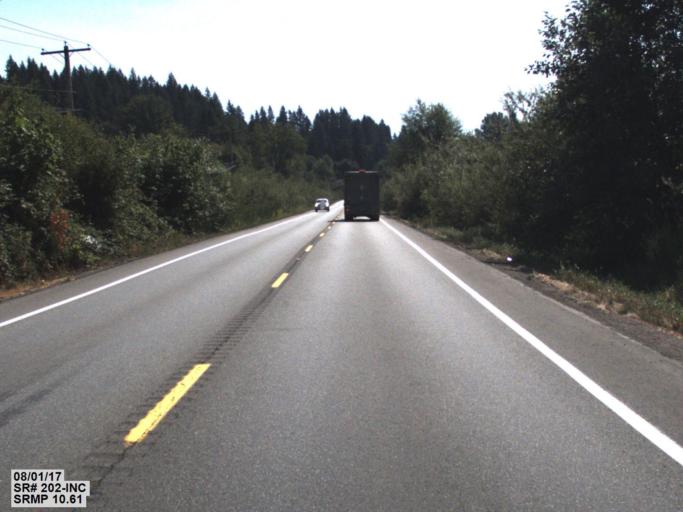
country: US
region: Washington
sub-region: King County
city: Sammamish
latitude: 47.6544
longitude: -122.0556
